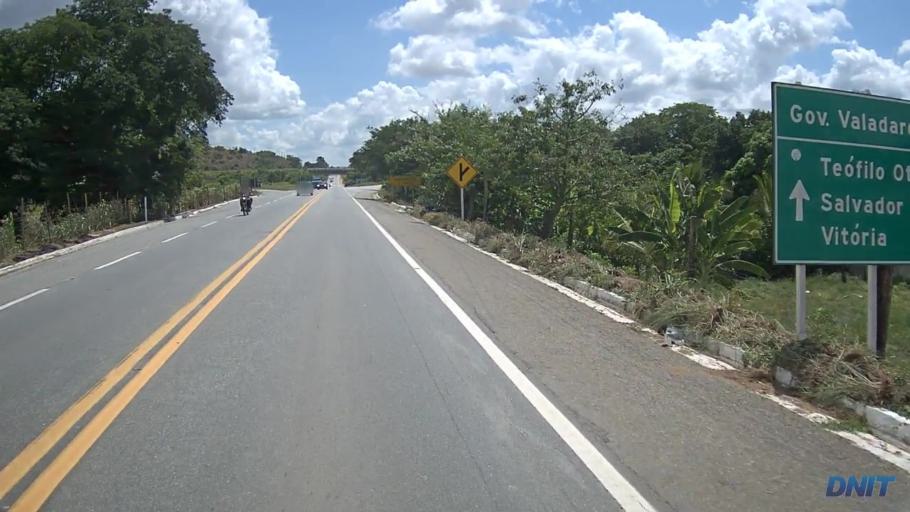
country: BR
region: Minas Gerais
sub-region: Governador Valadares
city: Governador Valadares
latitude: -18.9162
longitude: -42.0119
